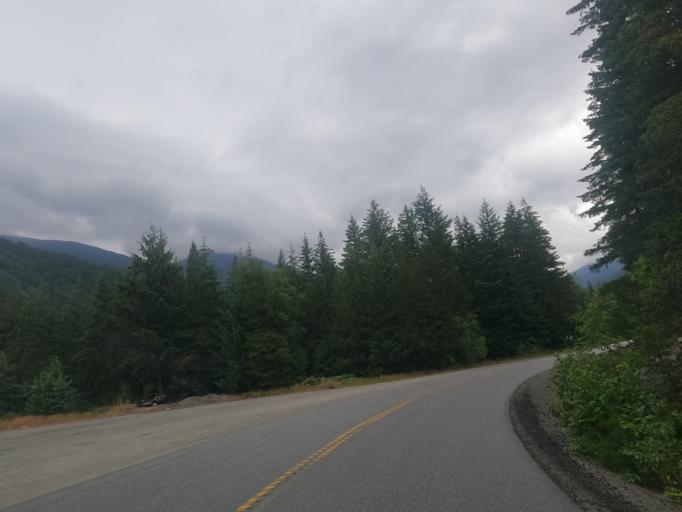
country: CA
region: British Columbia
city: Pemberton
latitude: 50.3075
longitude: -122.5787
